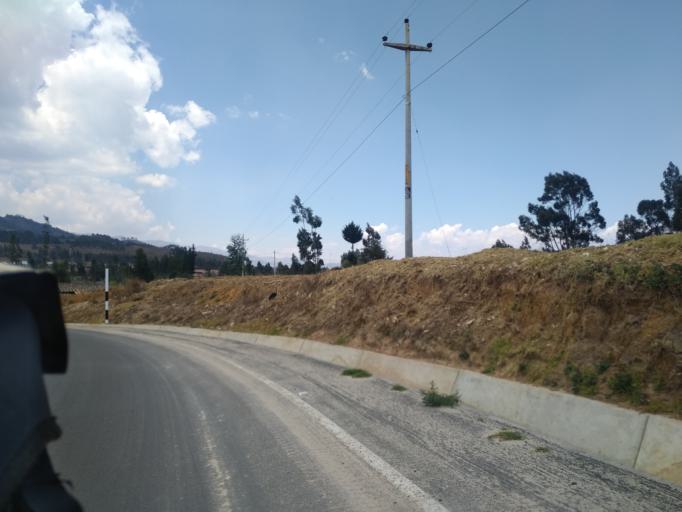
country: PE
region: Cajamarca
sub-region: San Marcos
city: San Marcos
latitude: -7.2825
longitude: -78.2259
